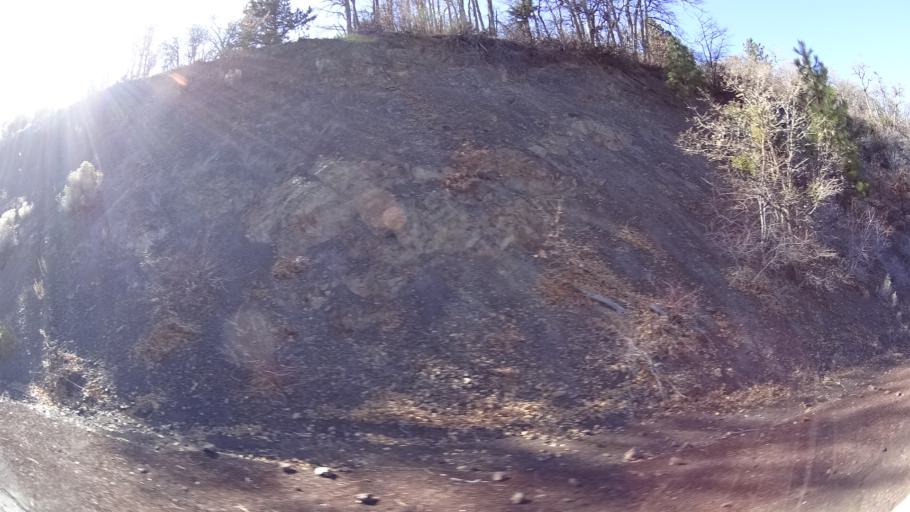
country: US
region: California
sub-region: Siskiyou County
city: Weed
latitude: 41.4382
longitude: -122.6399
